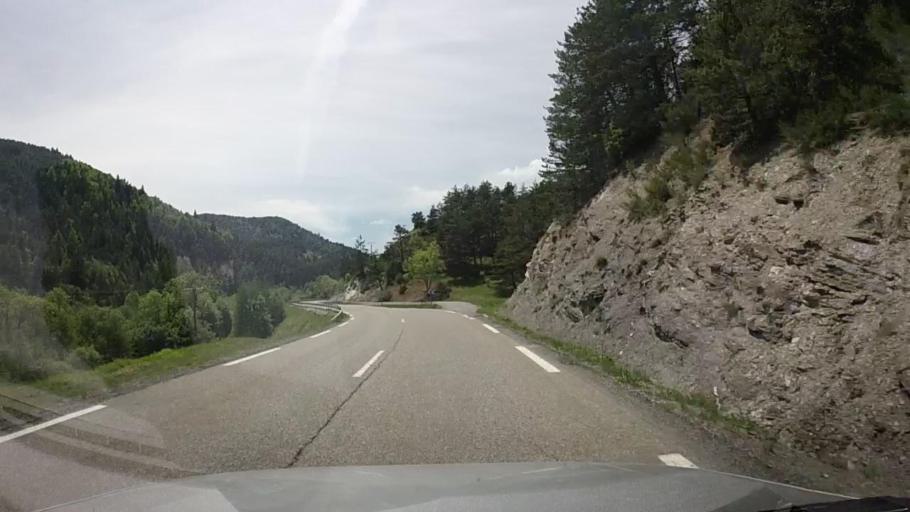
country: FR
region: Provence-Alpes-Cote d'Azur
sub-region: Departement des Alpes-de-Haute-Provence
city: Seyne-les-Alpes
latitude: 44.2724
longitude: 6.3822
